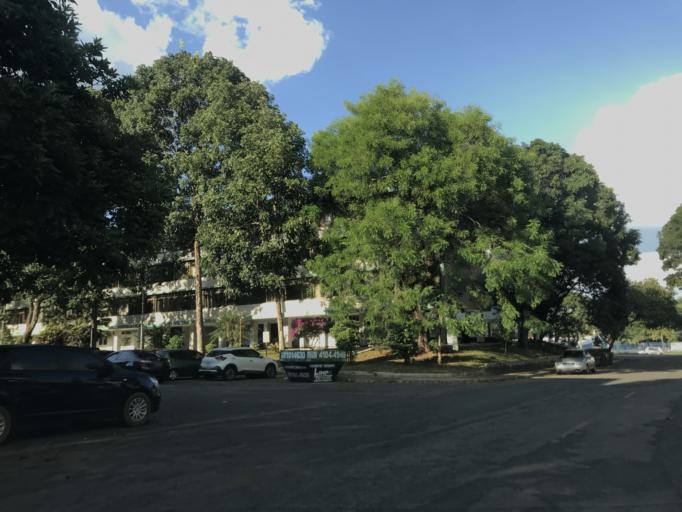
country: BR
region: Federal District
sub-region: Brasilia
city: Brasilia
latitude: -15.7747
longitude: -47.8757
